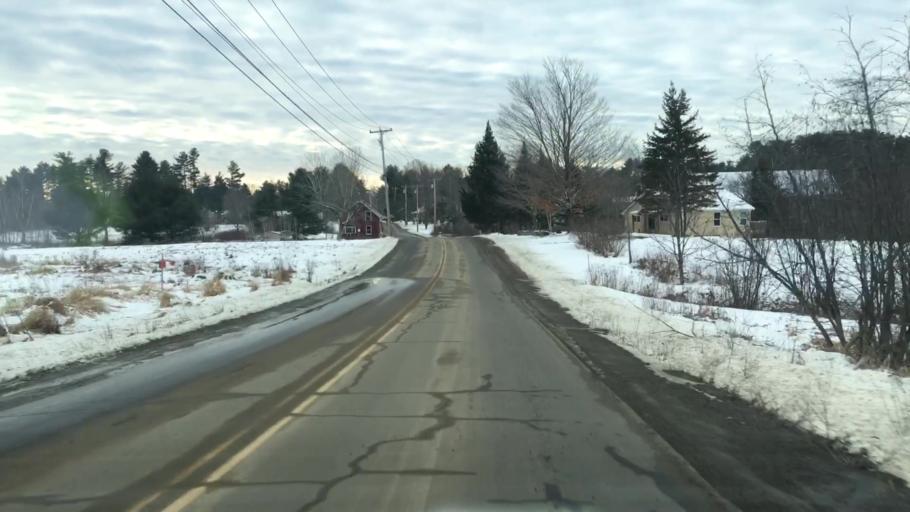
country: US
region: Maine
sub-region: Lincoln County
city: Whitefield
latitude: 44.2289
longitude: -69.5820
